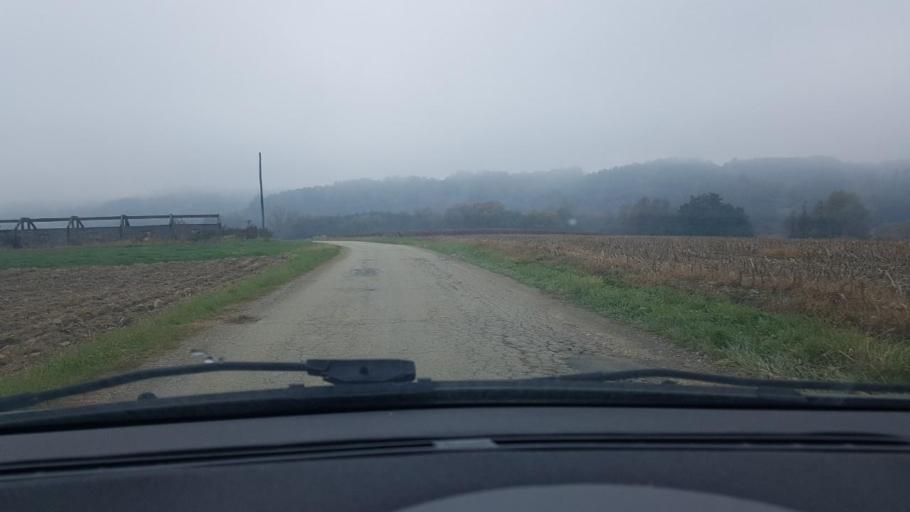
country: HR
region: Krapinsko-Zagorska
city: Zlatar
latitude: 46.1039
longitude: 16.1761
